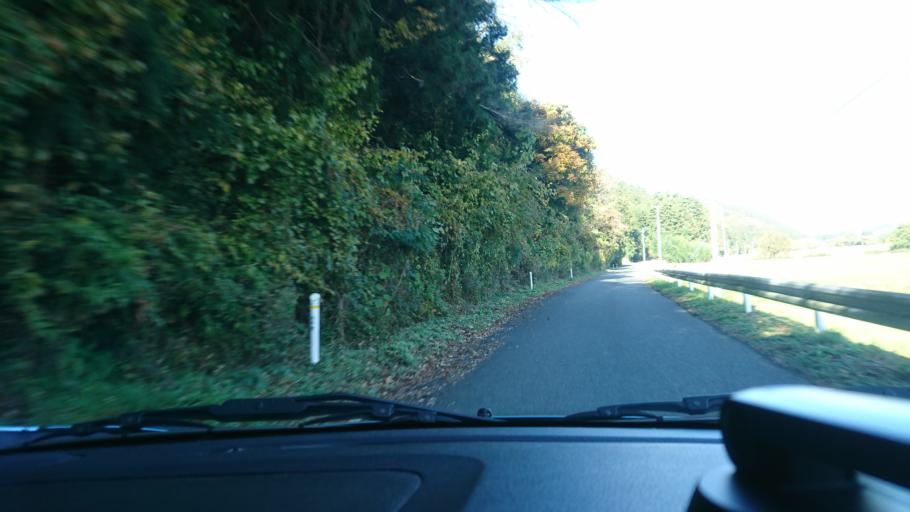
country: JP
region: Iwate
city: Ichinoseki
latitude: 38.8038
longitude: 141.2459
